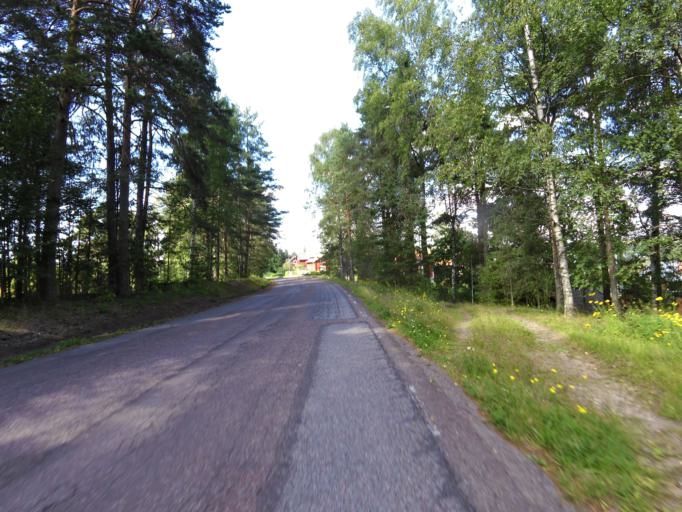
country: SE
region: Dalarna
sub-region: Faluns Kommun
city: Svardsjo
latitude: 60.6446
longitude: 15.8460
